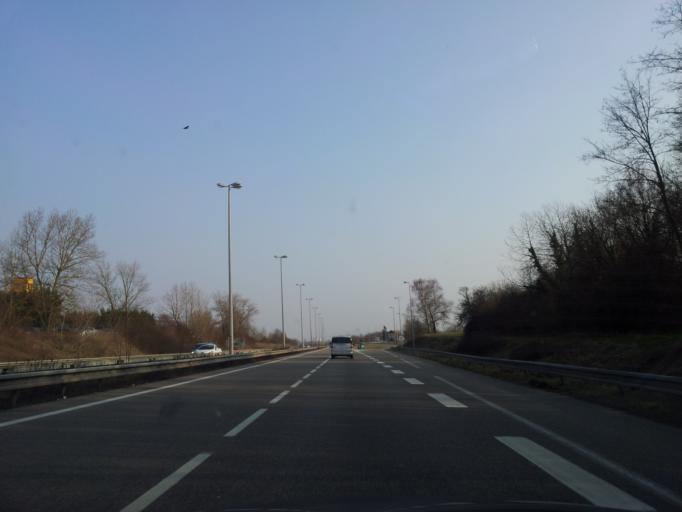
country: FR
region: Alsace
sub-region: Departement du Haut-Rhin
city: Rosenau
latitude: 47.6071
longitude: 7.5271
